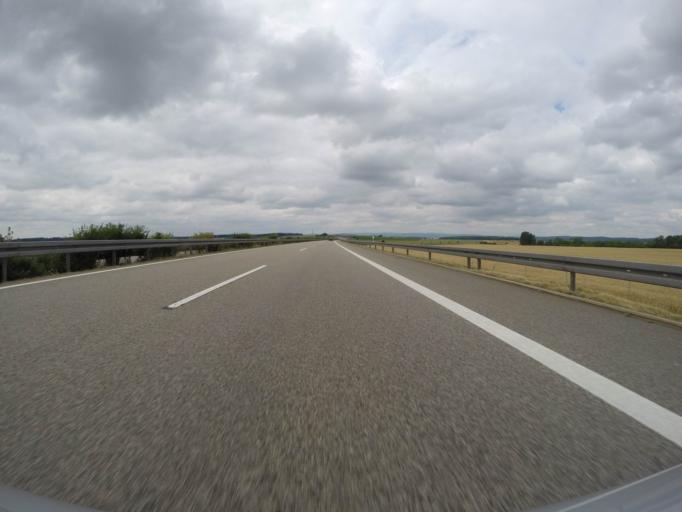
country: DE
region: Thuringia
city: Wolfershausen
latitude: 50.4290
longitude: 10.4074
